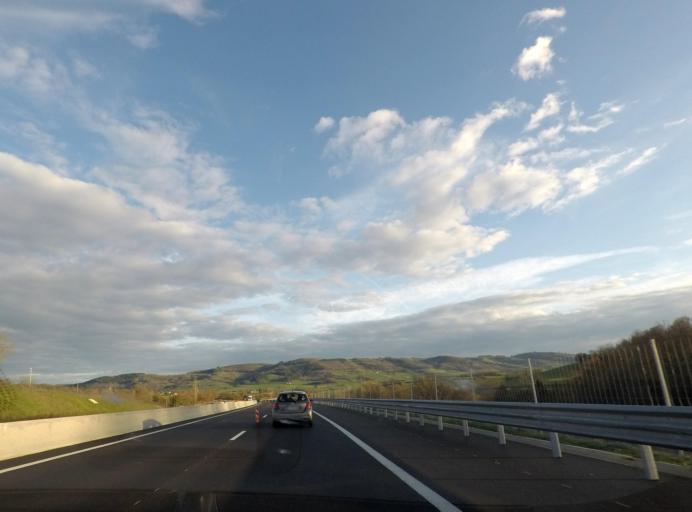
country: FR
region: Bourgogne
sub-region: Departement de Saone-et-Loire
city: Matour
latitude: 46.3689
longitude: 4.5562
